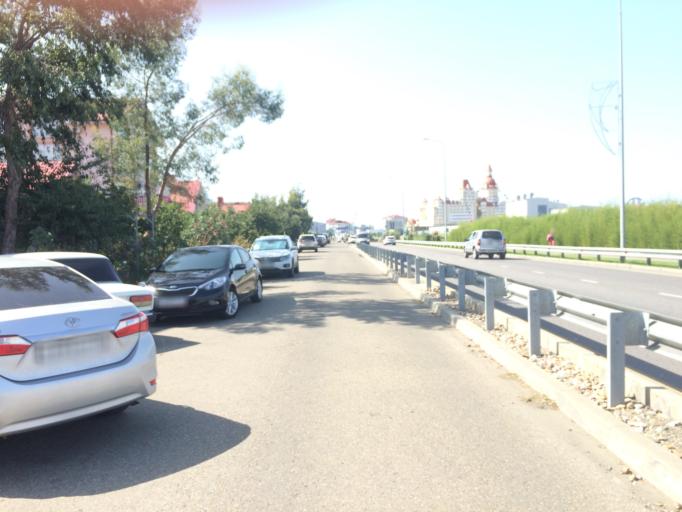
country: RU
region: Krasnodarskiy
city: Adler
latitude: 43.4001
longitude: 39.9699
